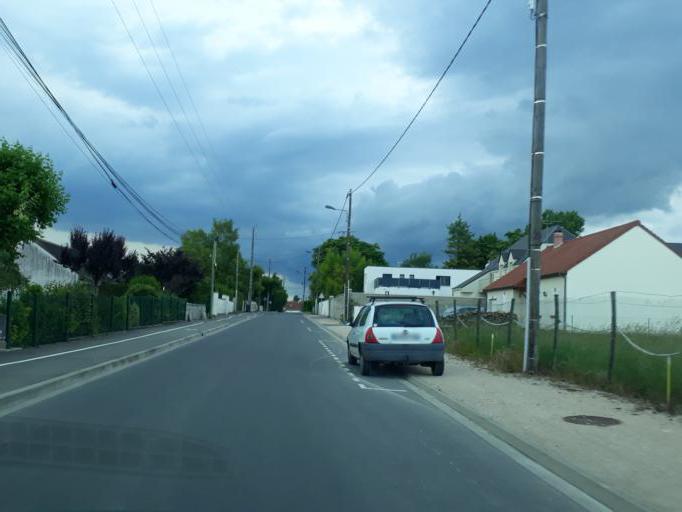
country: FR
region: Centre
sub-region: Departement du Loiret
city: Chaingy
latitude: 47.8863
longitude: 1.7879
